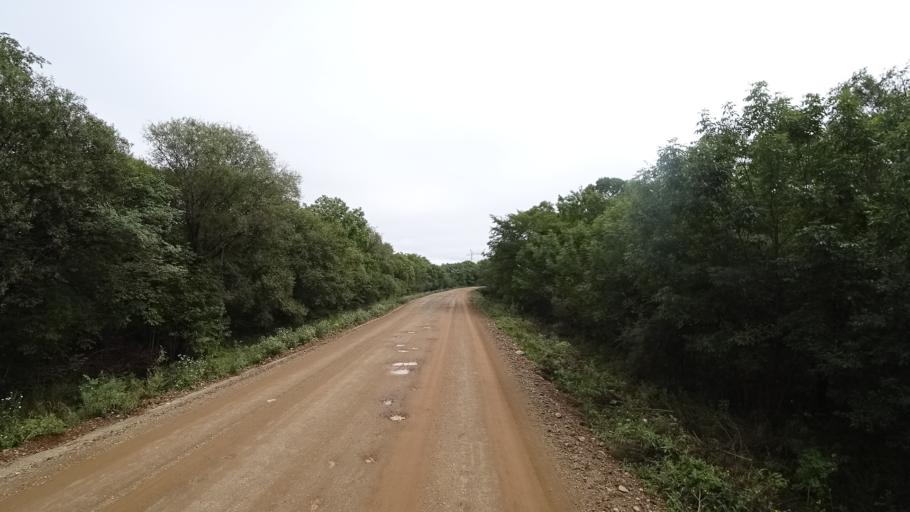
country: RU
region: Primorskiy
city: Lyalichi
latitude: 44.0818
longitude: 132.4491
